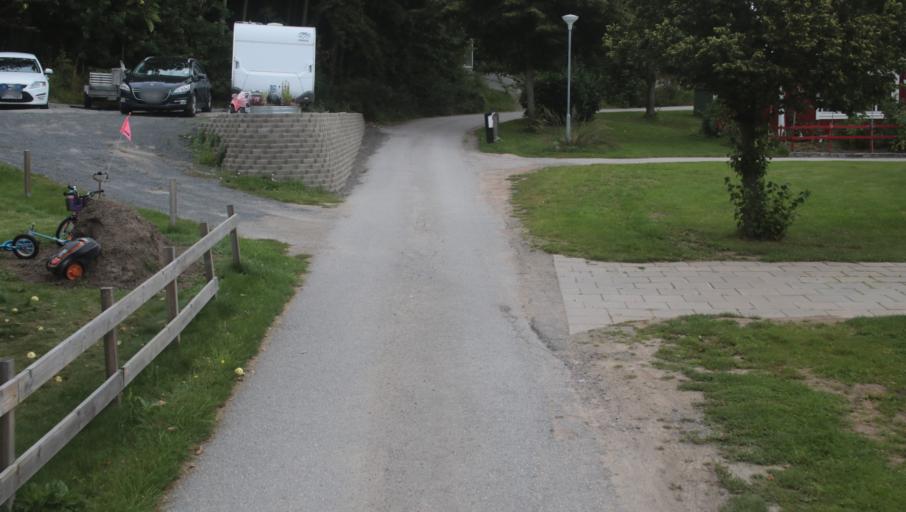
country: SE
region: Blekinge
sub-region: Ronneby Kommun
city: Brakne-Hoby
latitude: 56.2089
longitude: 15.0230
